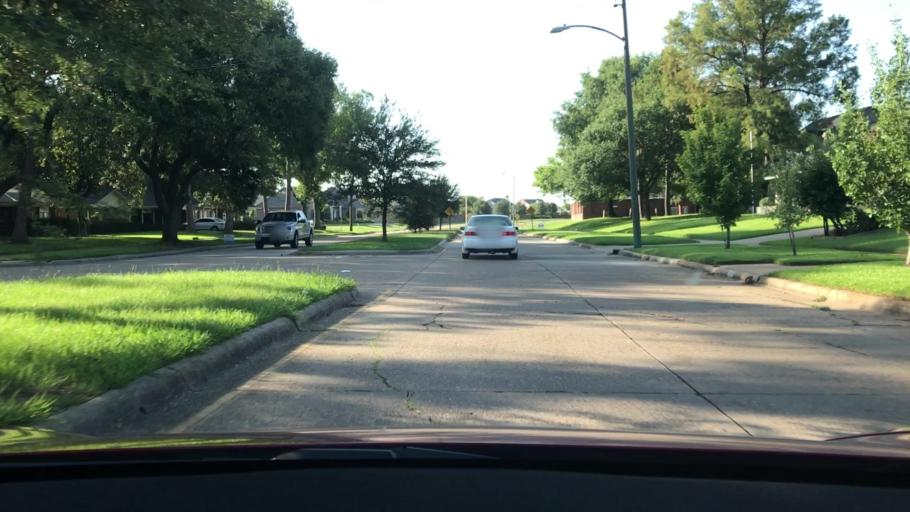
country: US
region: Louisiana
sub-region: Bossier Parish
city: Bossier City
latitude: 32.4530
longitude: -93.7323
